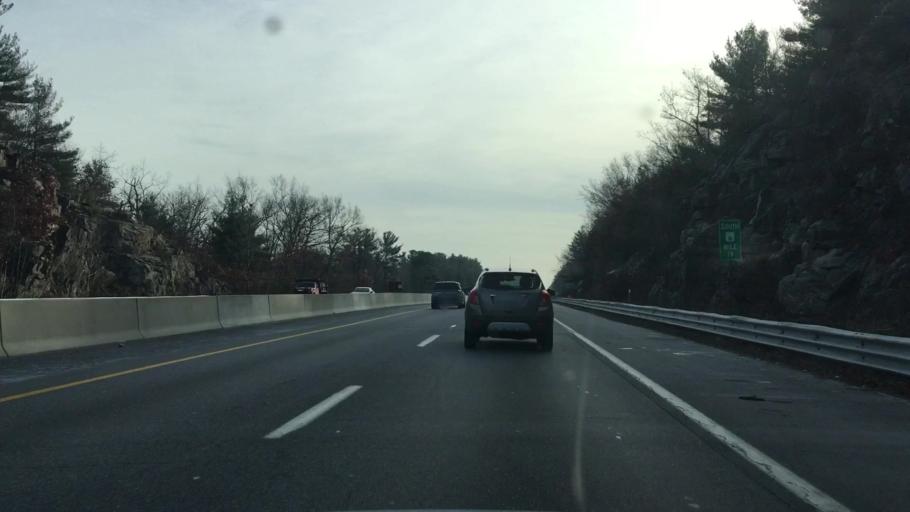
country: US
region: New Hampshire
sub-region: Hillsborough County
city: Bedford
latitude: 42.9408
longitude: -71.4699
